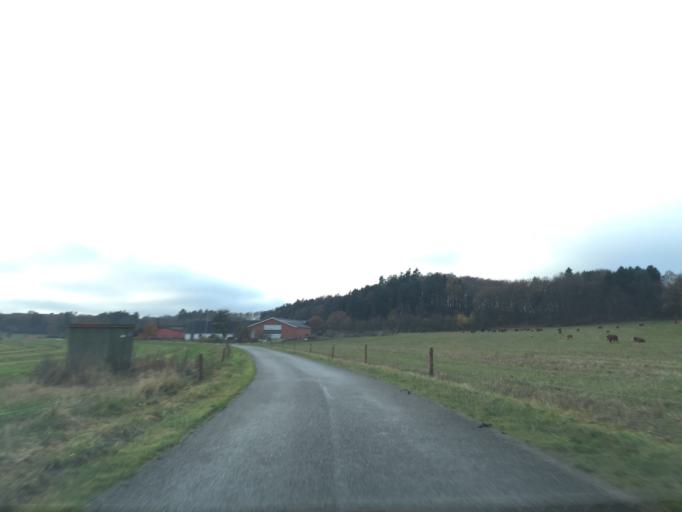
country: DK
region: Central Jutland
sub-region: Silkeborg Kommune
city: Svejbaek
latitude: 56.1679
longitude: 9.7094
